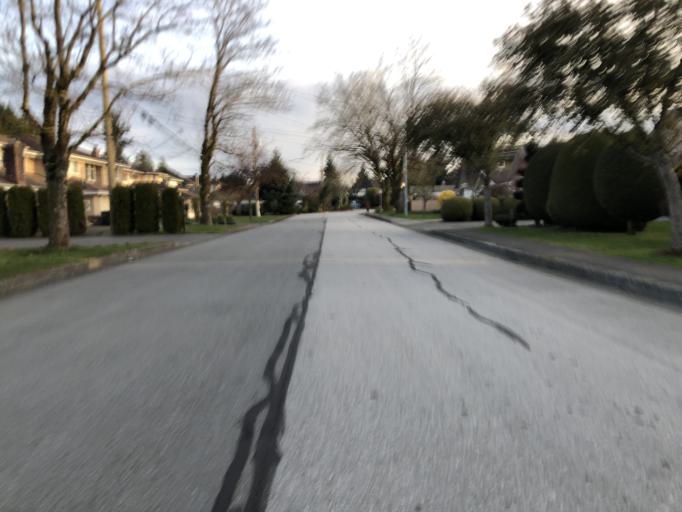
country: CA
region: British Columbia
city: Richmond
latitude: 49.1503
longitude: -123.1284
